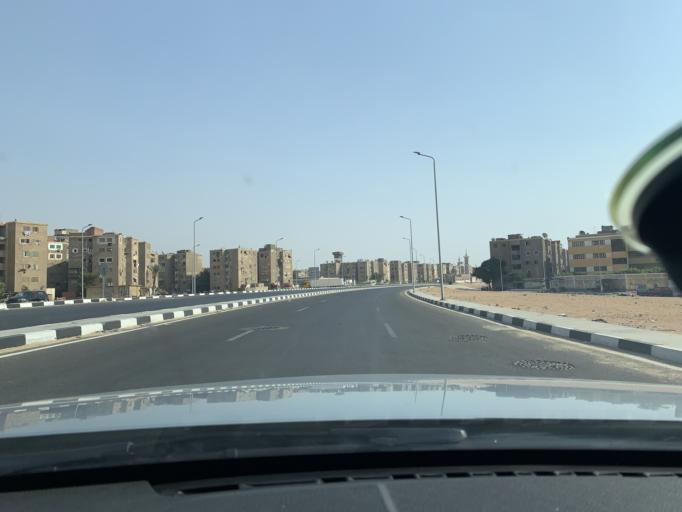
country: EG
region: Muhafazat al Qalyubiyah
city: Al Khankah
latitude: 30.1742
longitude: 31.4148
